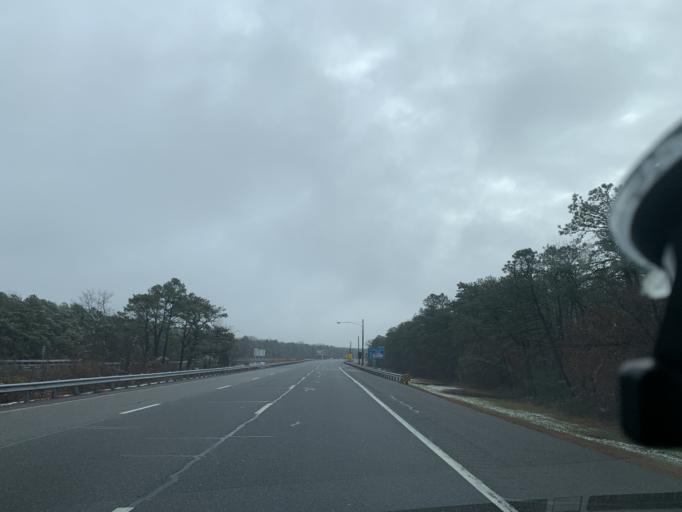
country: US
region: New Jersey
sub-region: Atlantic County
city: Pomona
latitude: 39.4378
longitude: -74.5956
